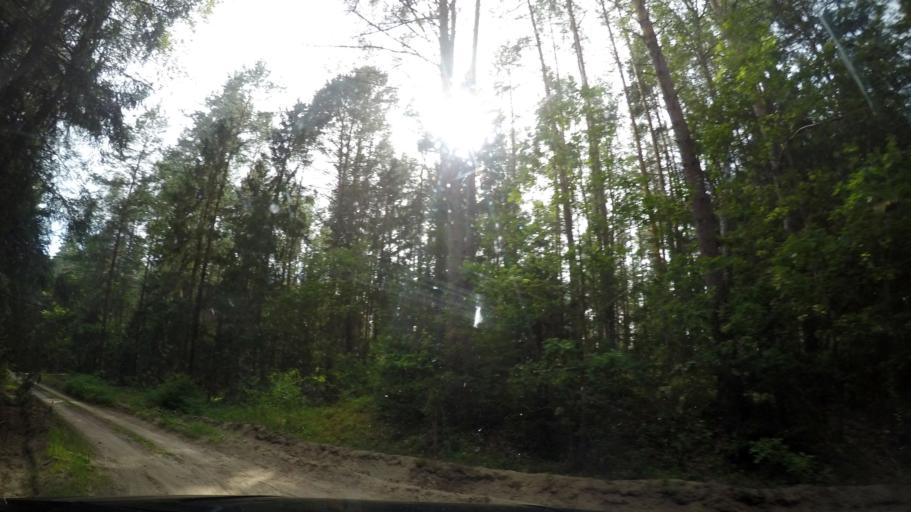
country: BY
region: Grodnenskaya
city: Skidal'
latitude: 53.8397
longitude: 24.1765
